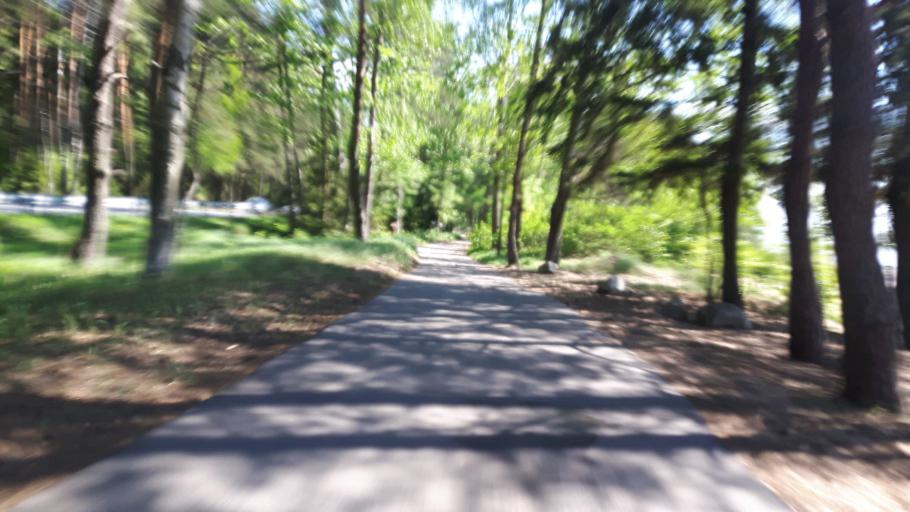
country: RU
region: St.-Petersburg
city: Komarovo
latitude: 60.1785
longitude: 29.7825
